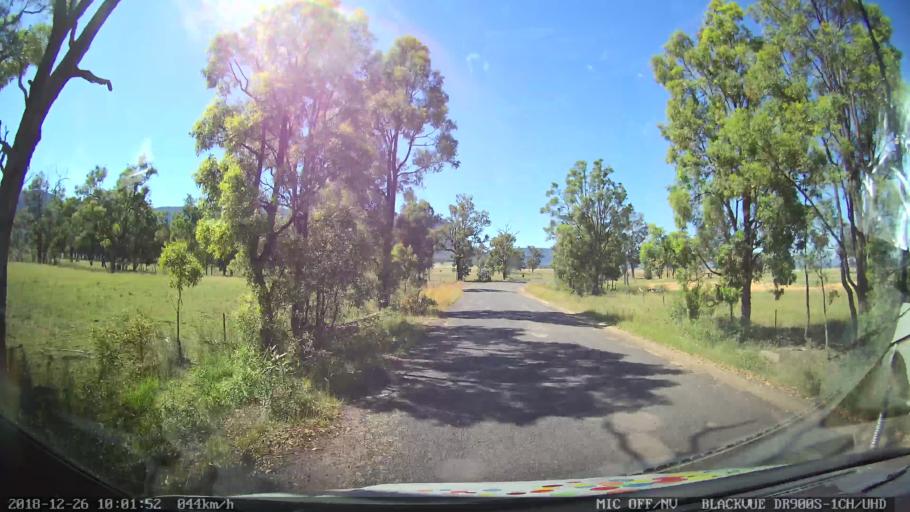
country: AU
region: New South Wales
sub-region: Mid-Western Regional
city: Kandos
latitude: -33.0499
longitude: 150.2229
